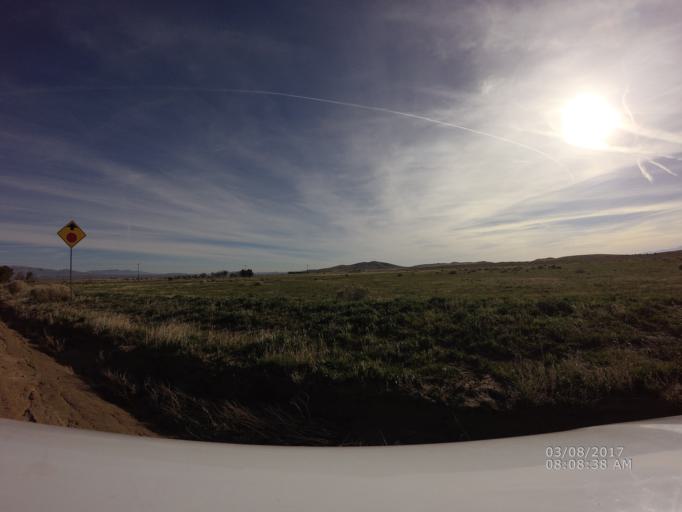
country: US
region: California
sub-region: Los Angeles County
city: Green Valley
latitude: 34.7372
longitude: -118.4487
